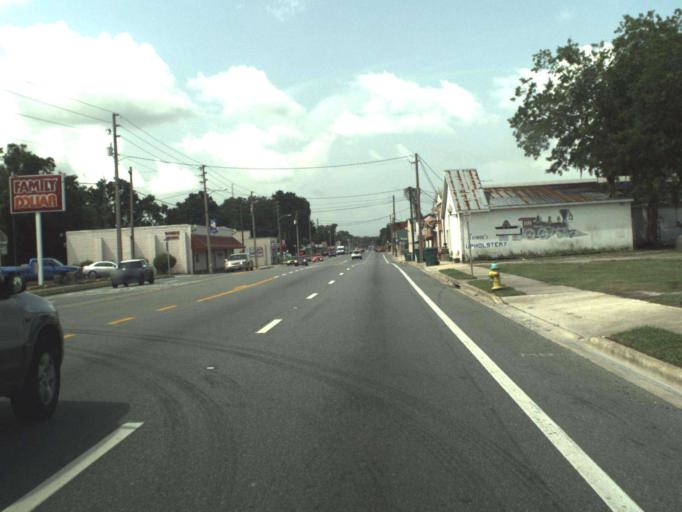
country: US
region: Florida
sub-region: Sumter County
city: Wildwood
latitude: 28.8652
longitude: -82.0399
